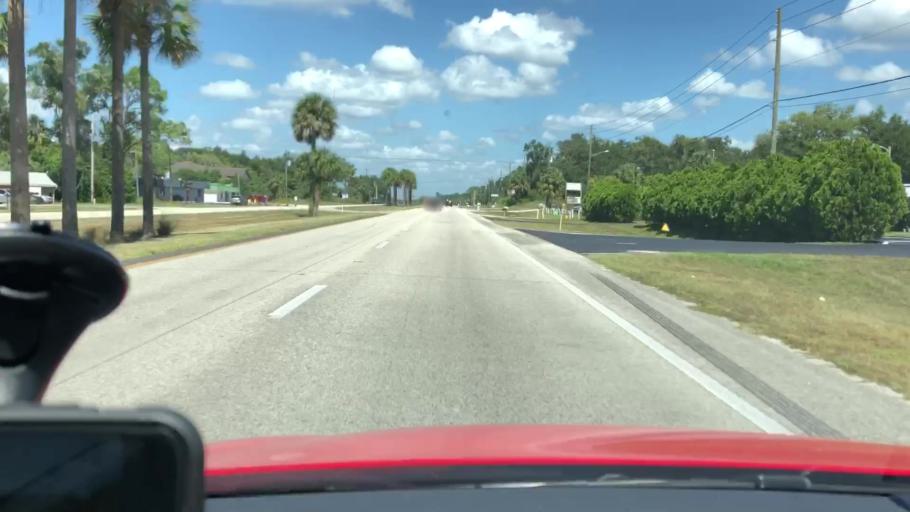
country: US
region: Florida
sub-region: Volusia County
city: Orange City
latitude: 28.9656
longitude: -81.2986
